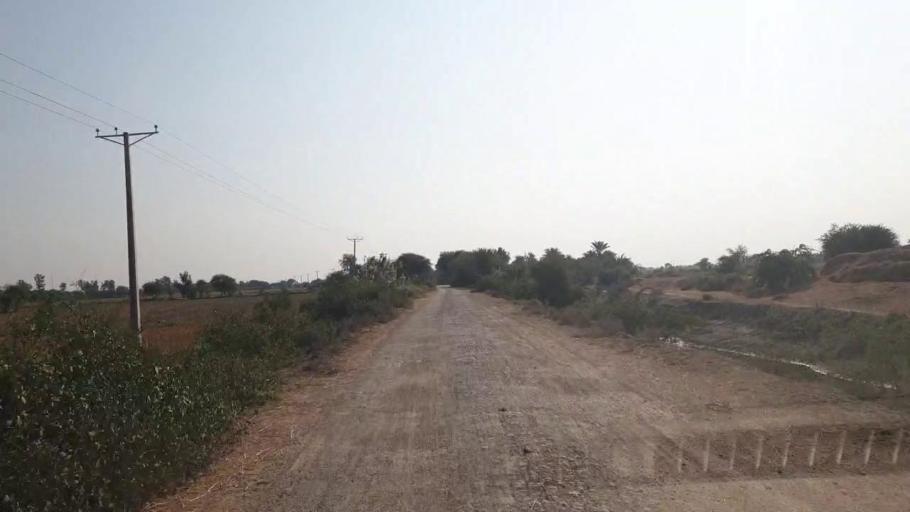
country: PK
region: Sindh
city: Kario
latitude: 24.8984
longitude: 68.6476
